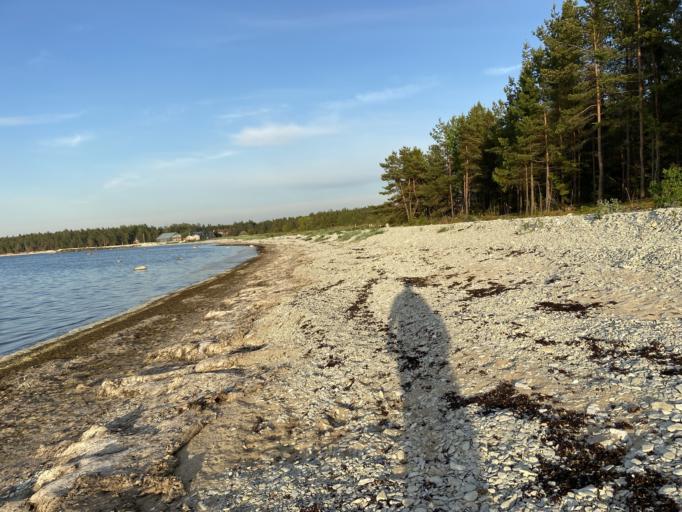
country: EE
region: Harju
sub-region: Paldiski linn
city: Paldiski
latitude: 59.2708
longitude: 23.7363
